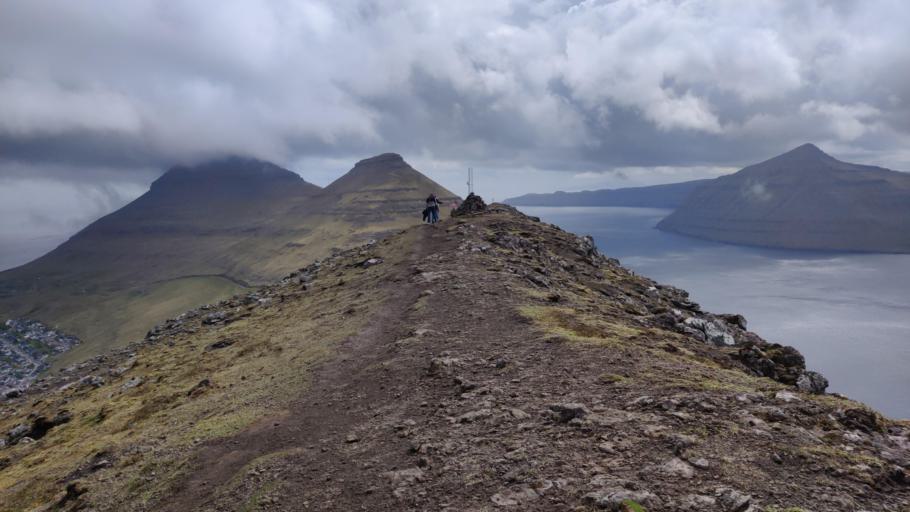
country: FO
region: Nordoyar
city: Klaksvik
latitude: 62.2365
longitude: -6.6173
